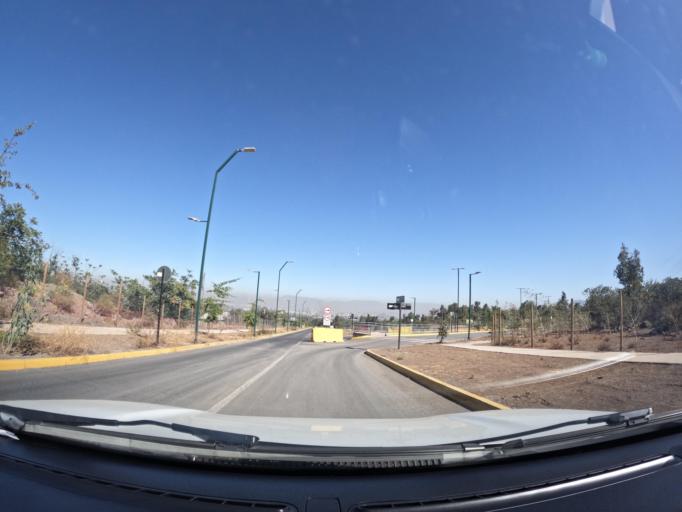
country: CL
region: Santiago Metropolitan
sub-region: Provincia de Santiago
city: Villa Presidente Frei, Nunoa, Santiago, Chile
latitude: -33.5032
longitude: -70.5322
